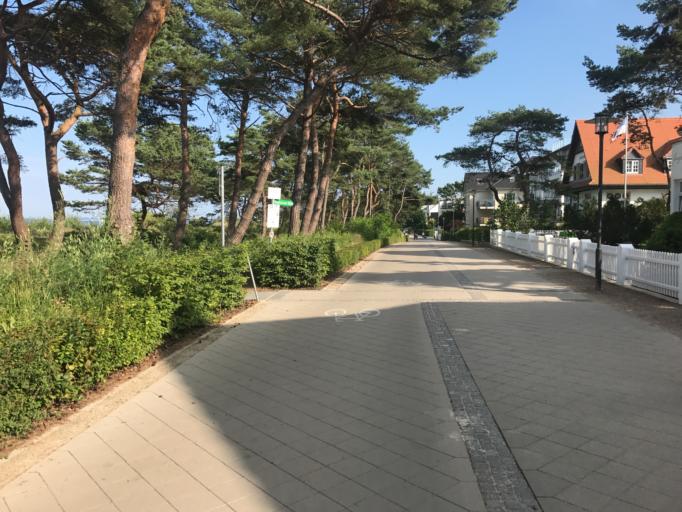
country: DE
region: Mecklenburg-Vorpommern
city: Seebad Bansin
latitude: 53.9689
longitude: 14.1500
